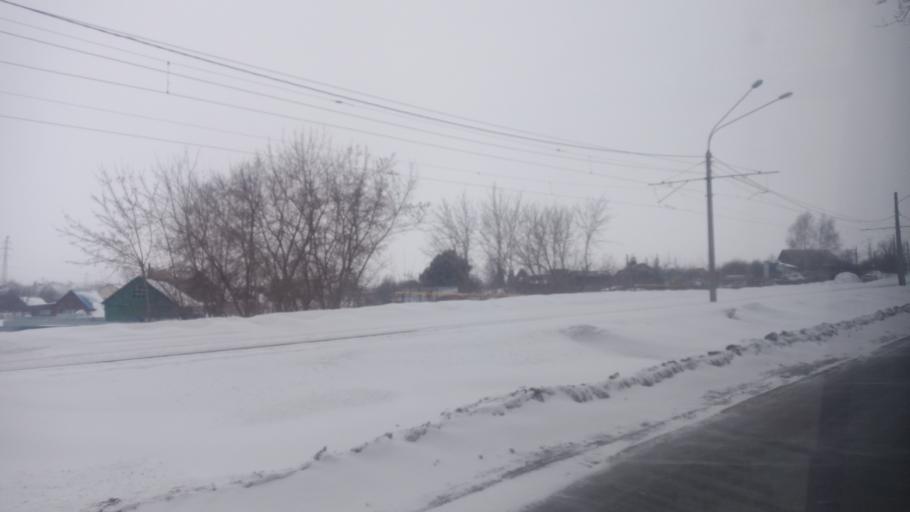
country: RU
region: Altai Krai
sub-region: Gorod Barnaulskiy
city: Barnaul
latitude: 53.3889
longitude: 83.6788
